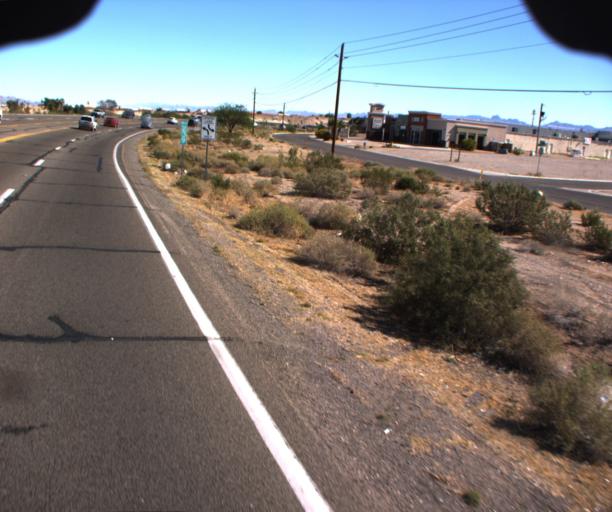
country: US
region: Arizona
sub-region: Mohave County
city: Mohave Valley
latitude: 35.0339
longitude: -114.5979
